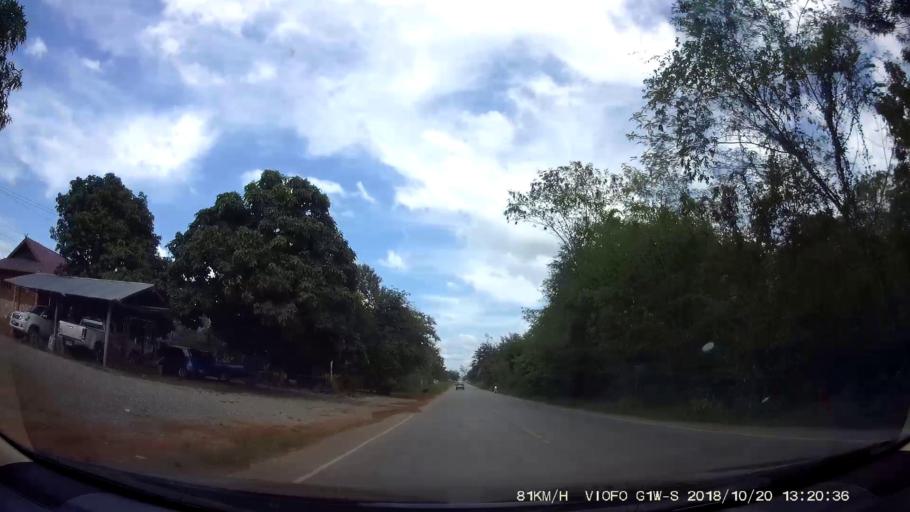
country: TH
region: Chaiyaphum
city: Khon San
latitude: 16.5499
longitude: 101.9050
